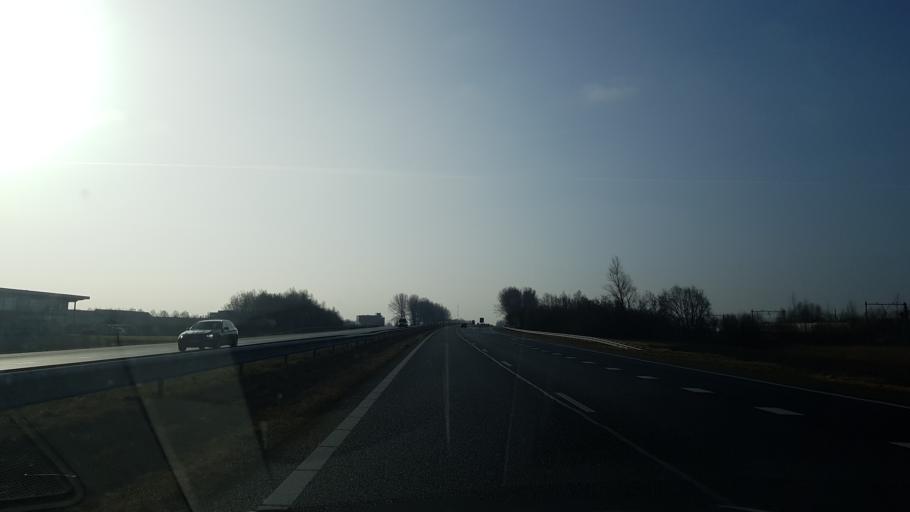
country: NL
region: Friesland
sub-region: Gemeente Boarnsterhim
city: Grou
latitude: 53.0958
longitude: 5.8205
